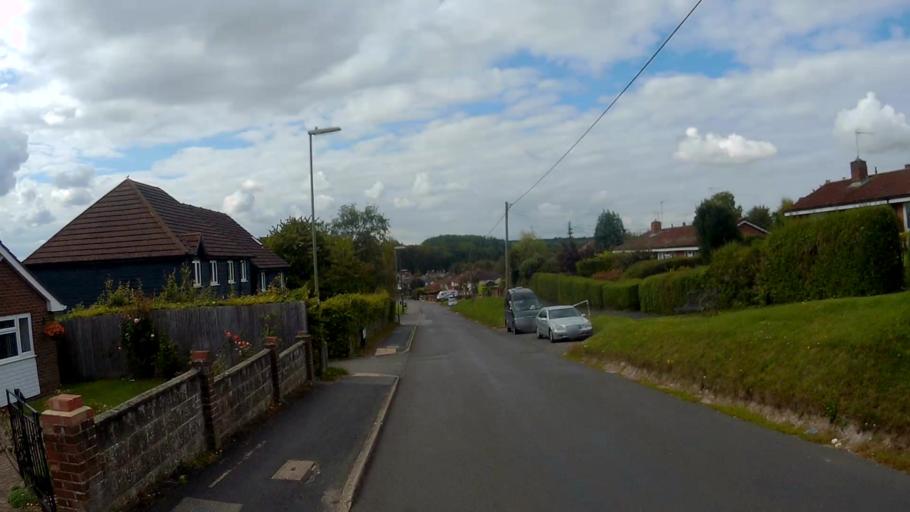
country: GB
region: England
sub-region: Hampshire
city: Overton
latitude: 51.2252
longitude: -1.3331
